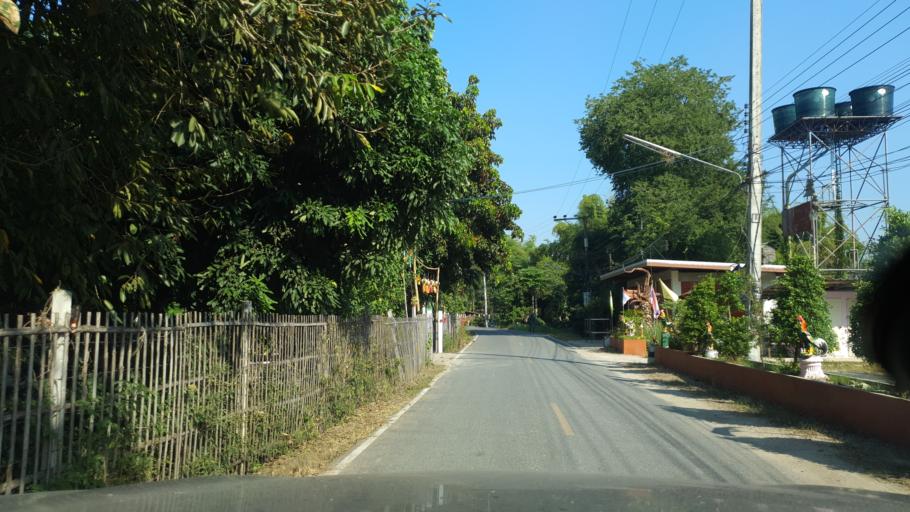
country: TH
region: Chiang Mai
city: Saraphi
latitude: 18.7039
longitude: 99.0762
